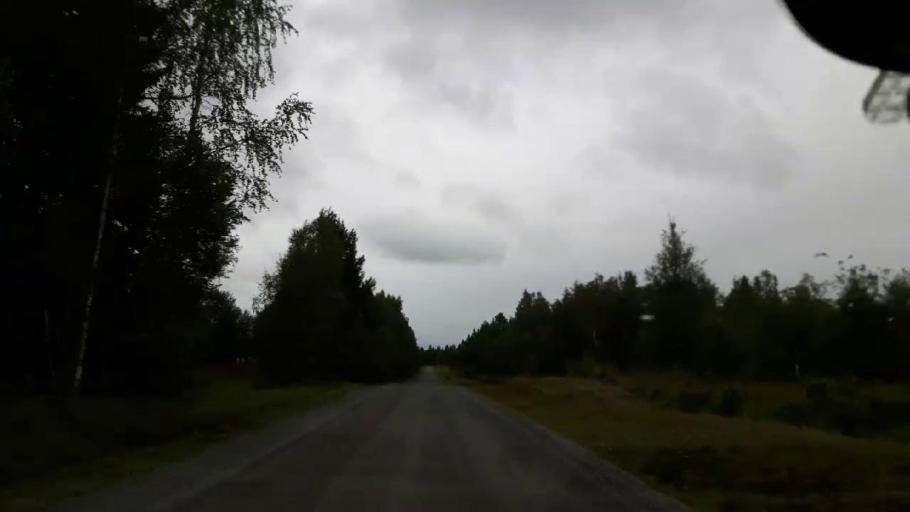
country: SE
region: Jaemtland
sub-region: OEstersunds Kommun
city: Ostersund
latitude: 63.0735
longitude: 14.5536
